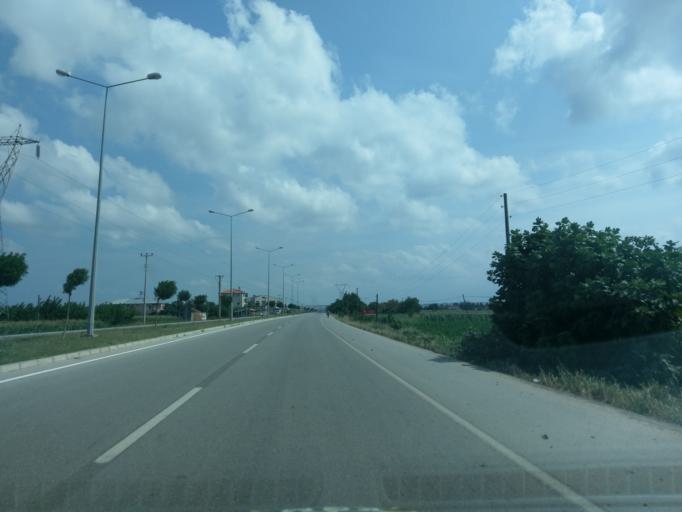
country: TR
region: Samsun
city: Bafra
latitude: 41.5775
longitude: 35.8533
